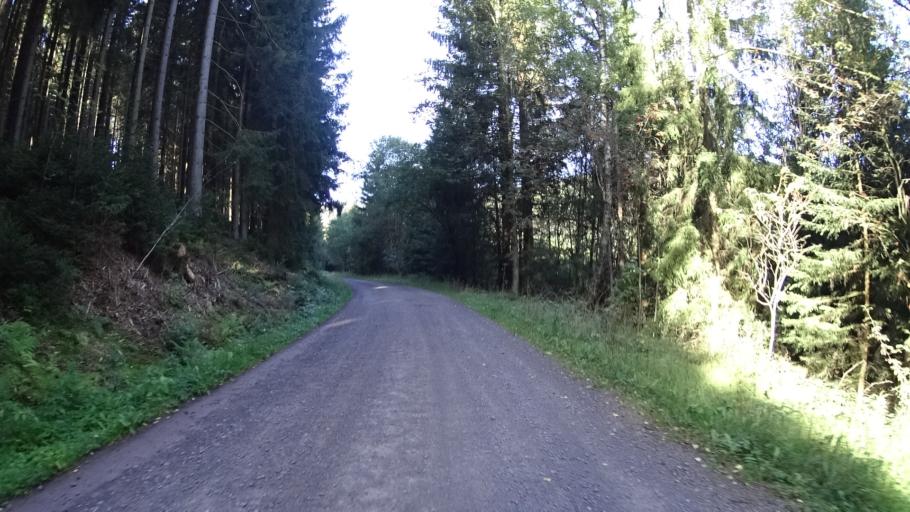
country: DE
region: Thuringia
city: Langewiesen
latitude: 50.6437
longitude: 10.9437
